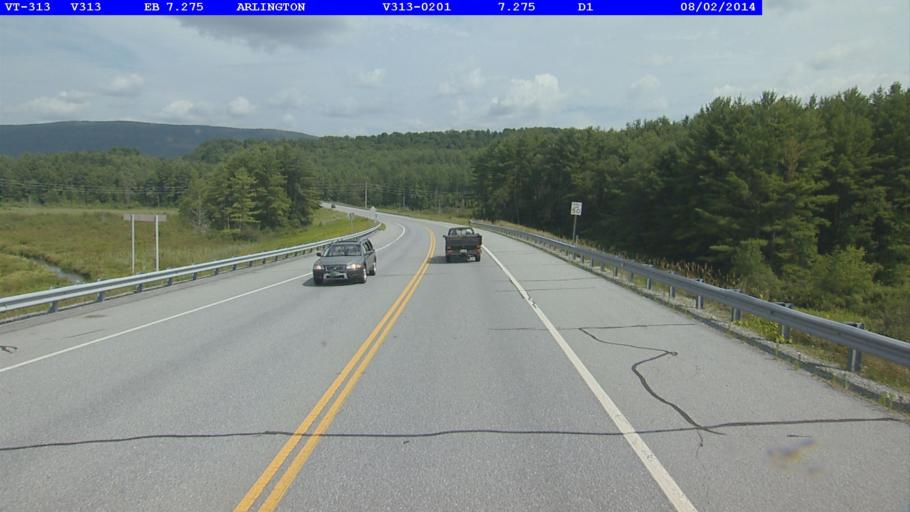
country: US
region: Vermont
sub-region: Bennington County
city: Arlington
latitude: 43.0535
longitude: -73.1509
